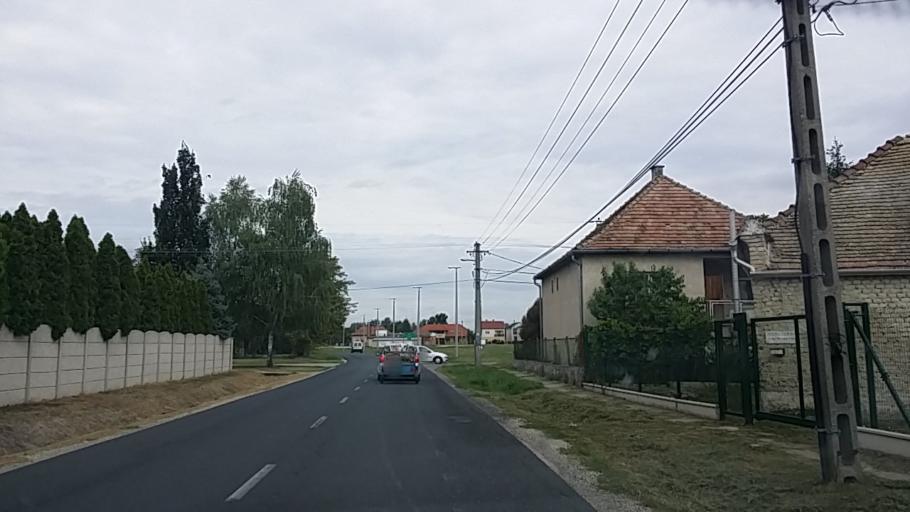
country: HU
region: Komarom-Esztergom
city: Komarom
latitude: 47.7327
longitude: 18.1574
